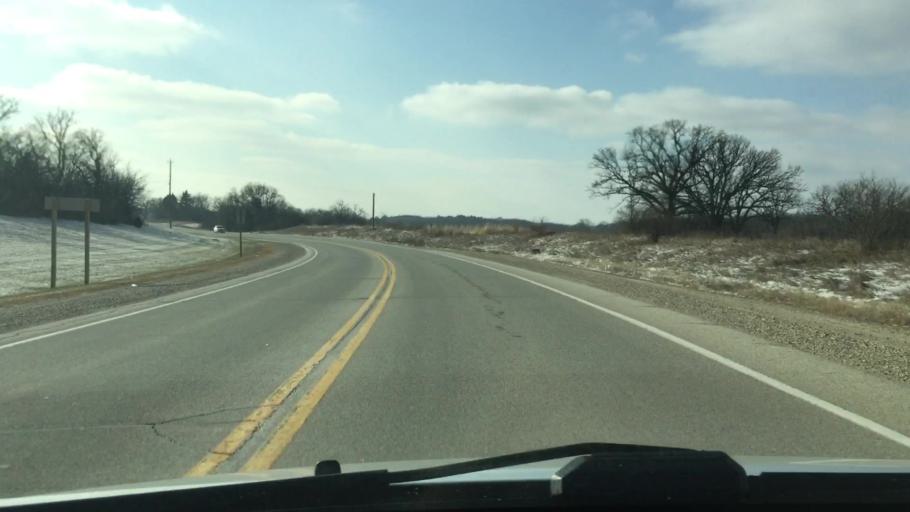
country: US
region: Wisconsin
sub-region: Waukesha County
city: North Prairie
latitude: 42.9294
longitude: -88.4262
